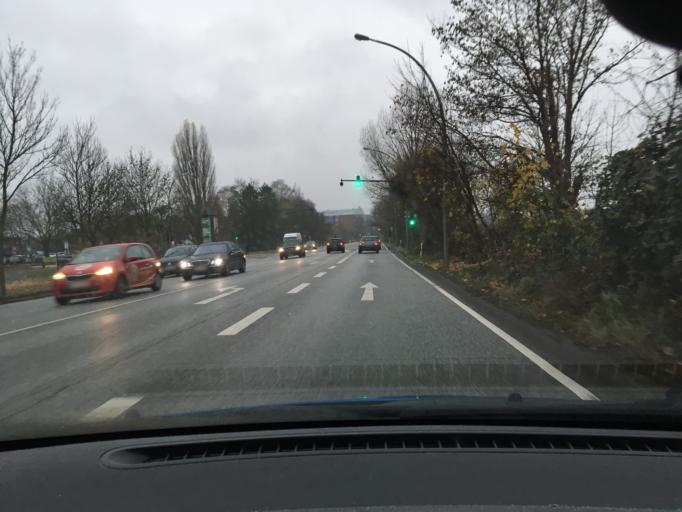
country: DE
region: Hamburg
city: Harburg
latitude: 53.4633
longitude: 10.0121
